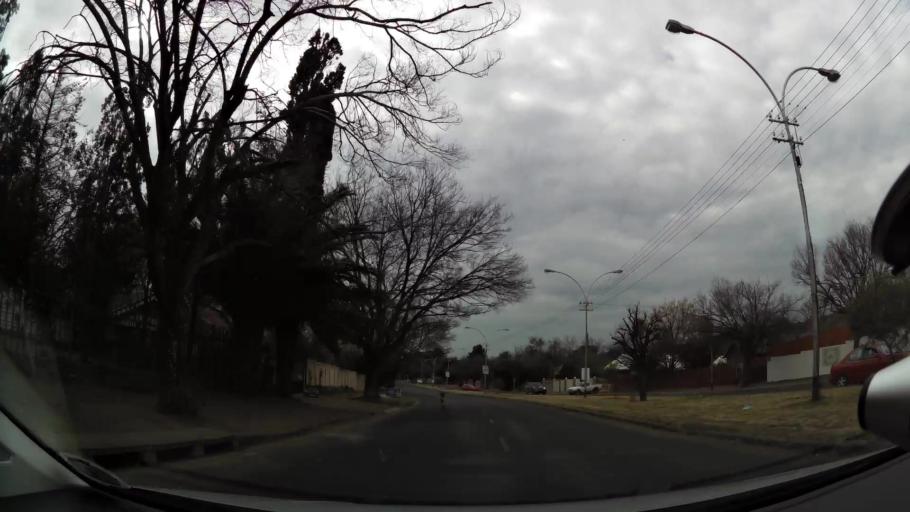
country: ZA
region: Orange Free State
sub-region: Mangaung Metropolitan Municipality
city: Bloemfontein
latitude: -29.0947
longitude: 26.2142
